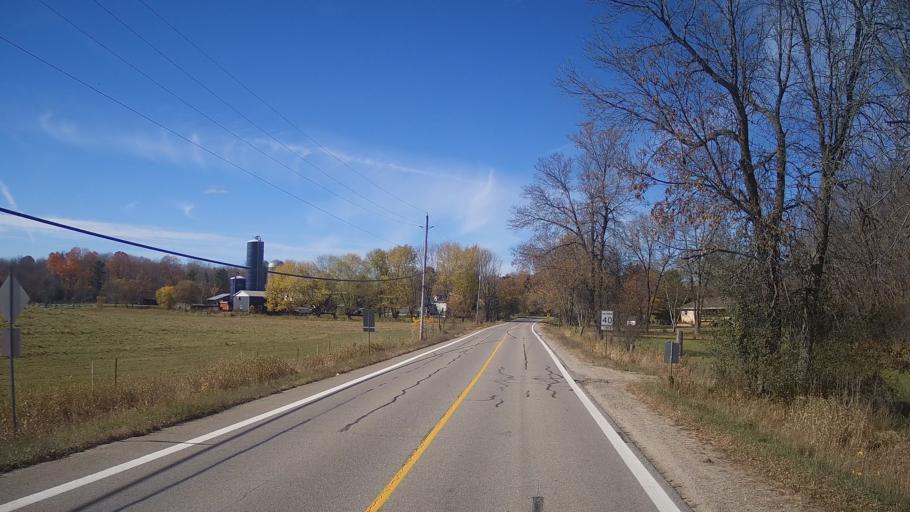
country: CA
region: Ontario
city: Perth
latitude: 44.8749
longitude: -76.3002
